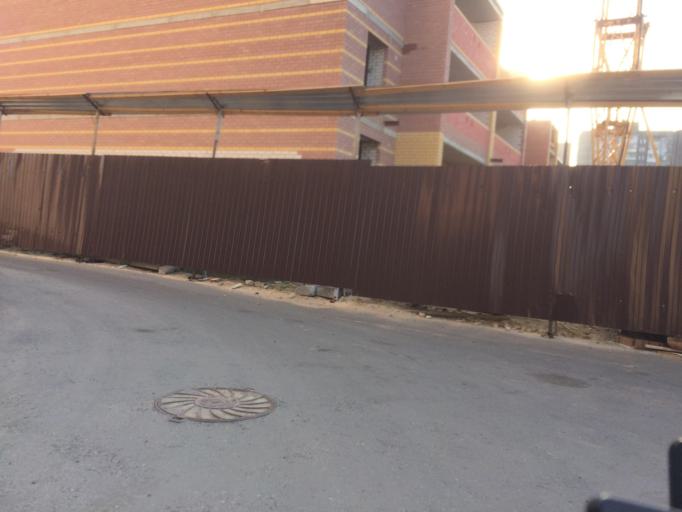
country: RU
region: Mariy-El
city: Yoshkar-Ola
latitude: 56.6406
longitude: 47.8555
